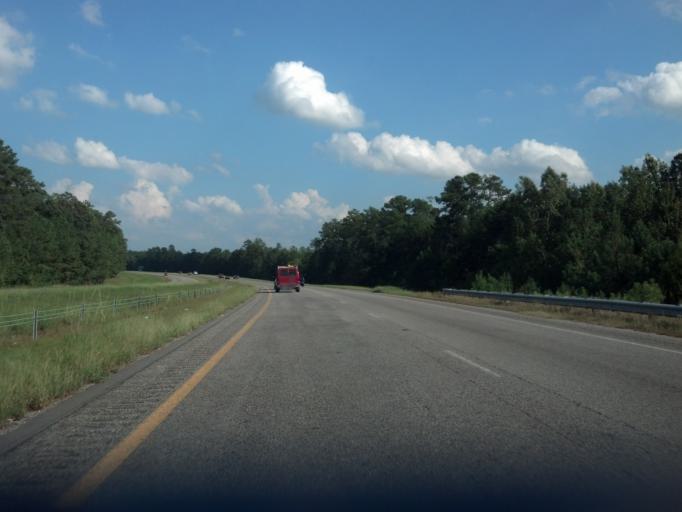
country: US
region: North Carolina
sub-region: Edgecombe County
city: Tarboro
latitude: 35.8985
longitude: -77.6362
